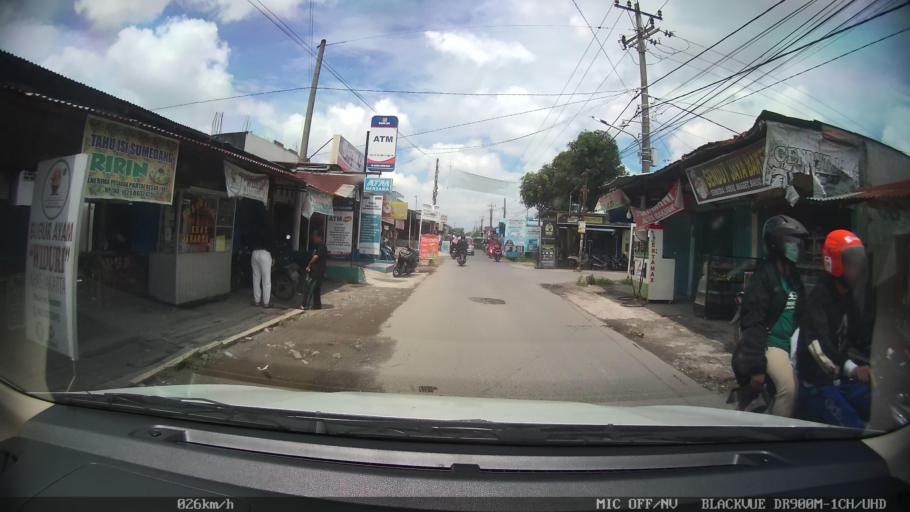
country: ID
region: North Sumatra
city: Medan
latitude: 3.6072
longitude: 98.7529
